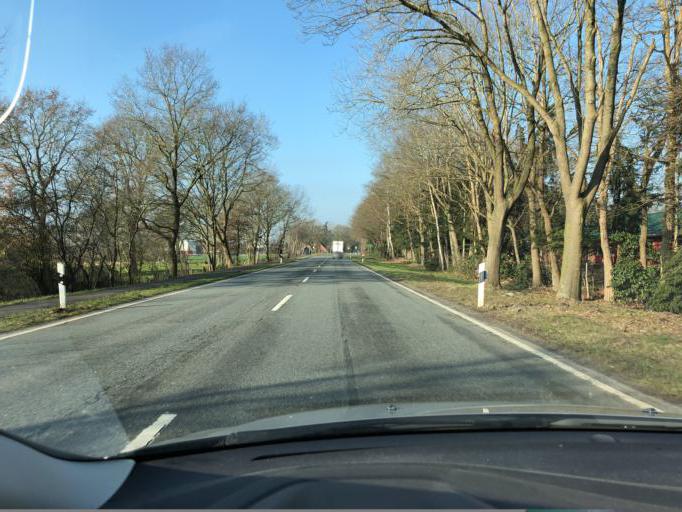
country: DE
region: Lower Saxony
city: Westerstede
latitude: 53.2919
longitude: 7.8788
